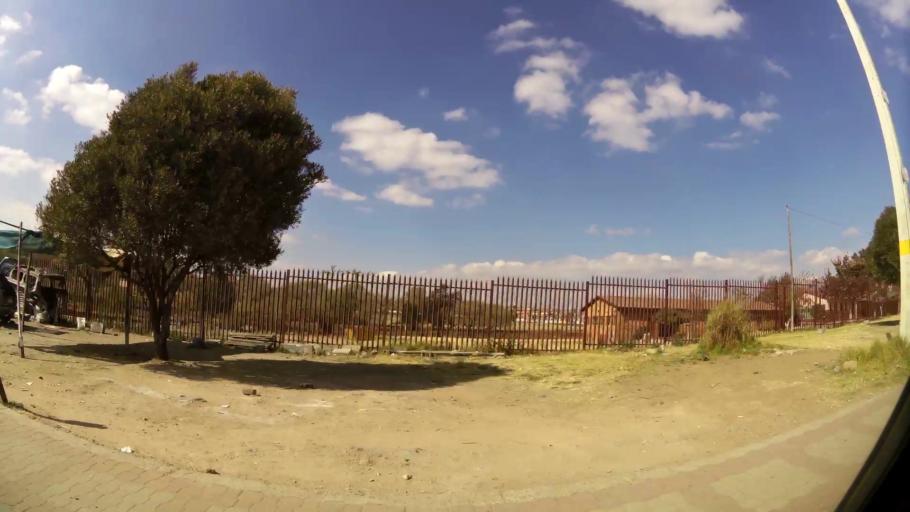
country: ZA
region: Gauteng
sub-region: Ekurhuleni Metropolitan Municipality
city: Tembisa
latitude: -26.0146
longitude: 28.2009
